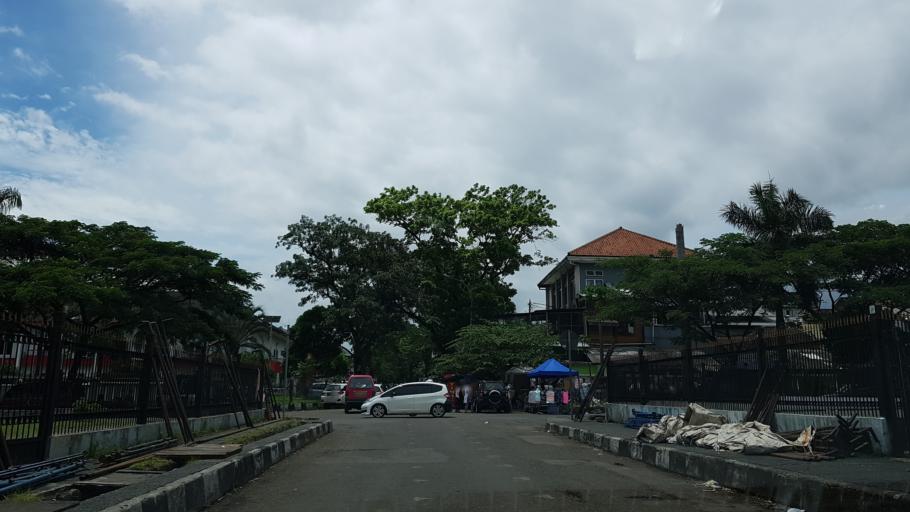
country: ID
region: West Java
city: Bandung
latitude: -6.8983
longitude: 107.6188
